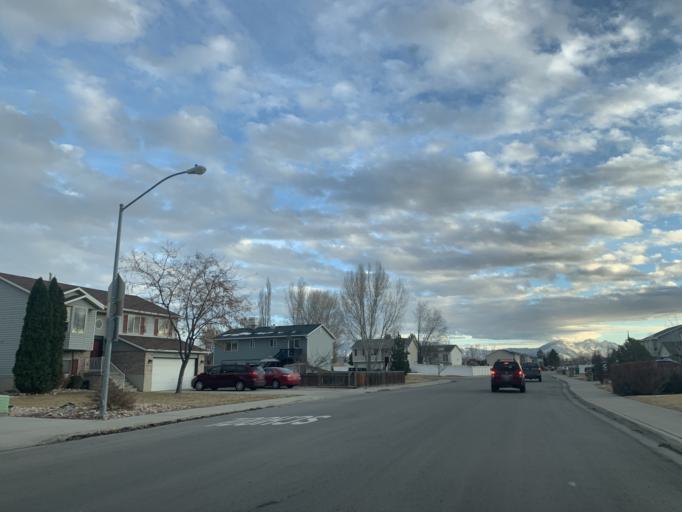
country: US
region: Utah
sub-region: Utah County
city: Orem
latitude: 40.2493
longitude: -111.7075
